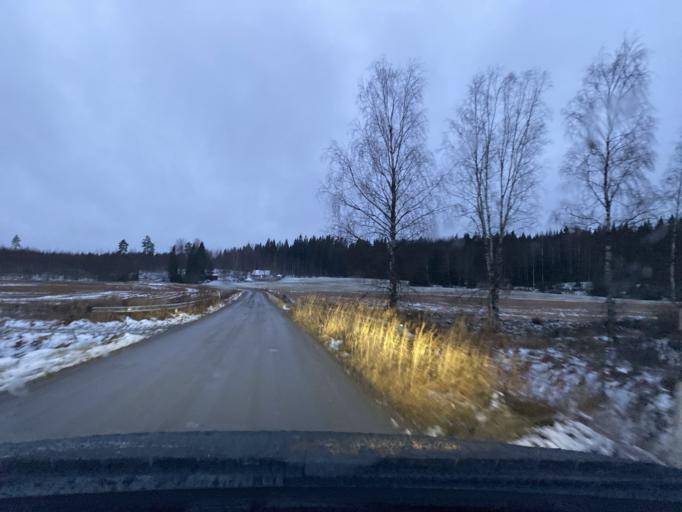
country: FI
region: Pirkanmaa
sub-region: Lounais-Pirkanmaa
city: Punkalaidun
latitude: 61.1613
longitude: 22.9609
